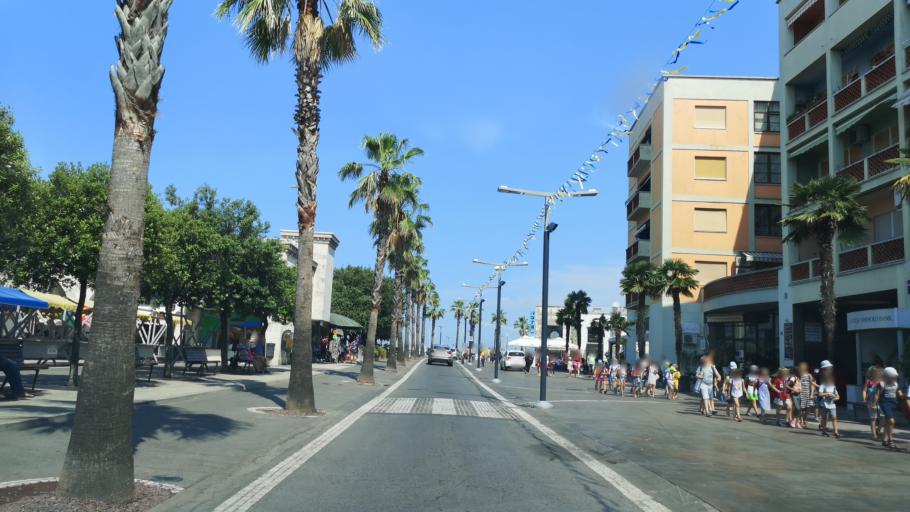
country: SI
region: Koper-Capodistria
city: Koper
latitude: 45.5463
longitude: 13.7265
